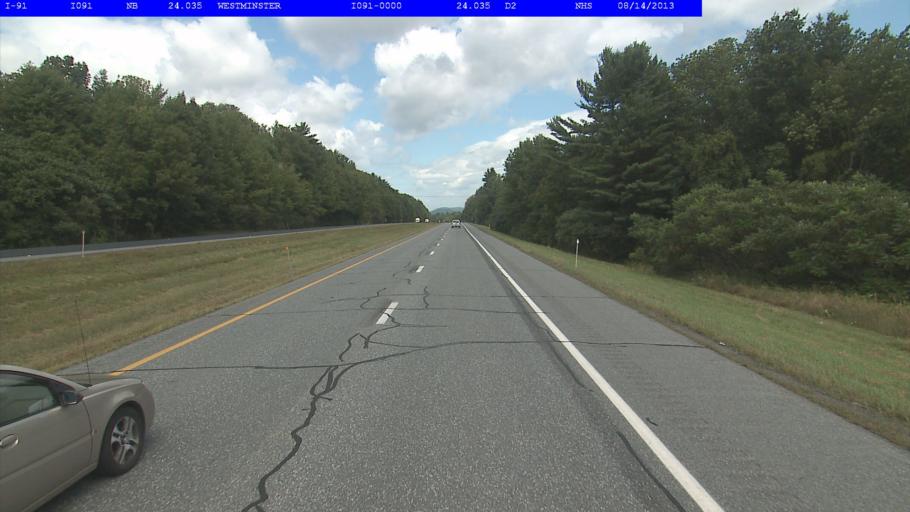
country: US
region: New Hampshire
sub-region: Cheshire County
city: Westmoreland
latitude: 43.0272
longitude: -72.4710
